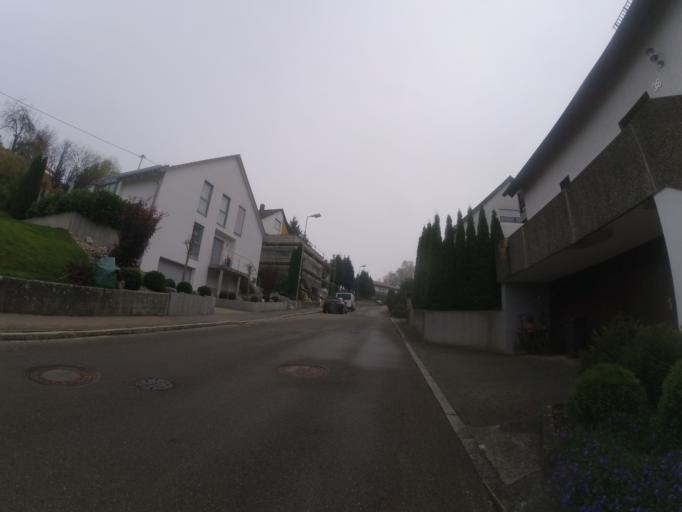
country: DE
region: Baden-Wuerttemberg
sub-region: Tuebingen Region
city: Staig
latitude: 48.3359
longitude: 10.0040
